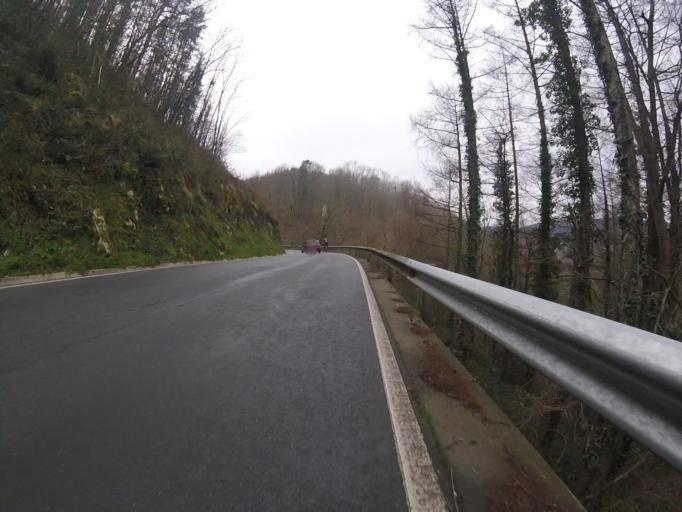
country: ES
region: Navarre
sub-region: Provincia de Navarra
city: Arantza
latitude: 43.2034
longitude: -1.7147
